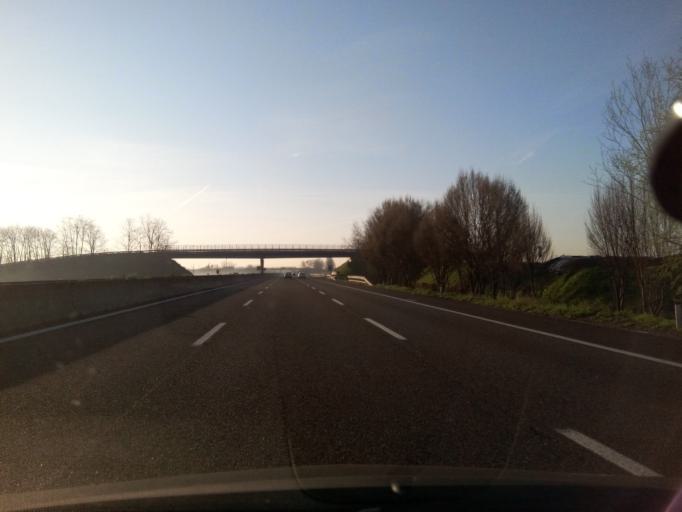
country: IT
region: Lombardy
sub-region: Provincia di Lodi
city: Guardamiglio
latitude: 45.1215
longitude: 9.6713
